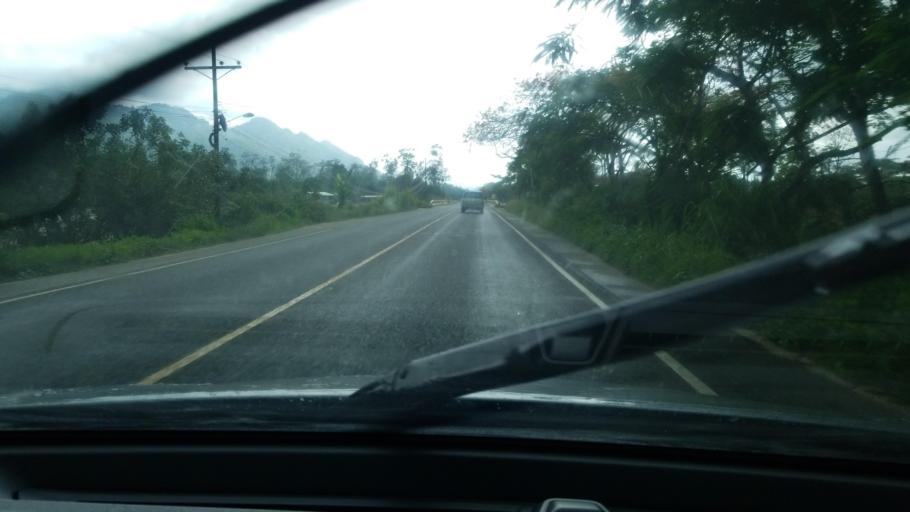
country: HN
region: Cortes
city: Rio Chiquito
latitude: 15.6307
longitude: -88.2493
